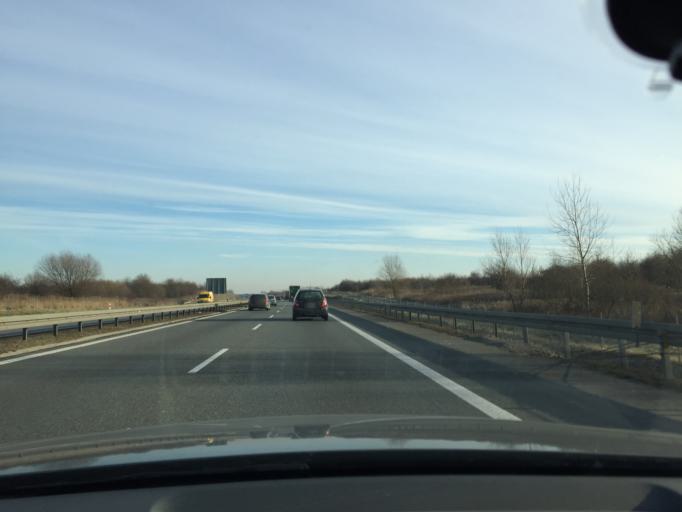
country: PL
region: Lesser Poland Voivodeship
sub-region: Krakow
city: Sidzina
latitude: 49.9923
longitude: 19.8757
